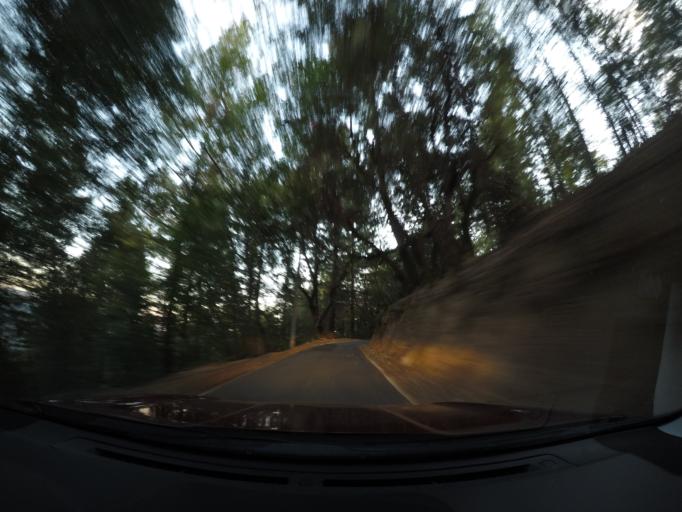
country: US
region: California
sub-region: Santa Clara County
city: Monte Sereno
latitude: 37.1881
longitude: -122.0315
